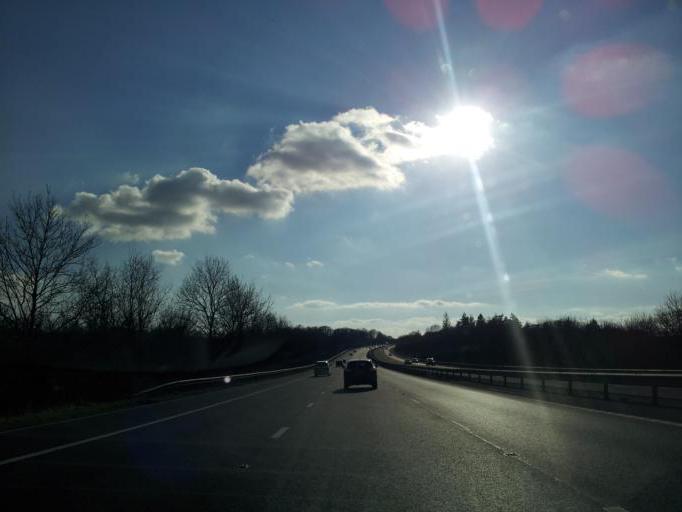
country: GB
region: England
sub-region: Devon
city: Uffculme
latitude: 50.9441
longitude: -3.2854
